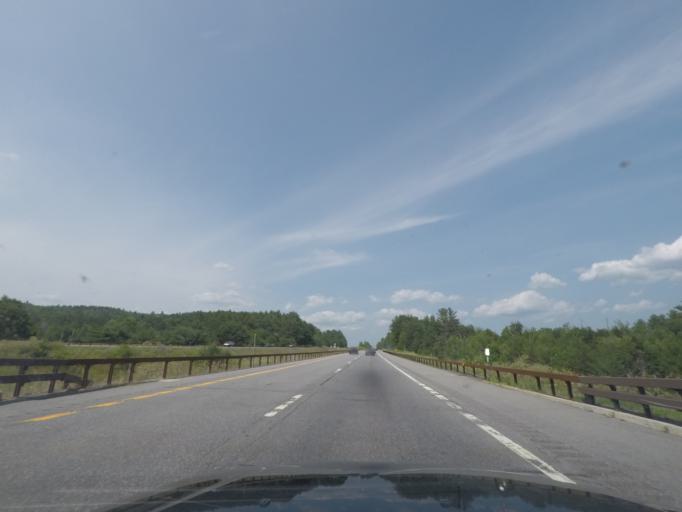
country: US
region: New York
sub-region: Warren County
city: Warrensburg
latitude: 43.7803
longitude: -73.7984
